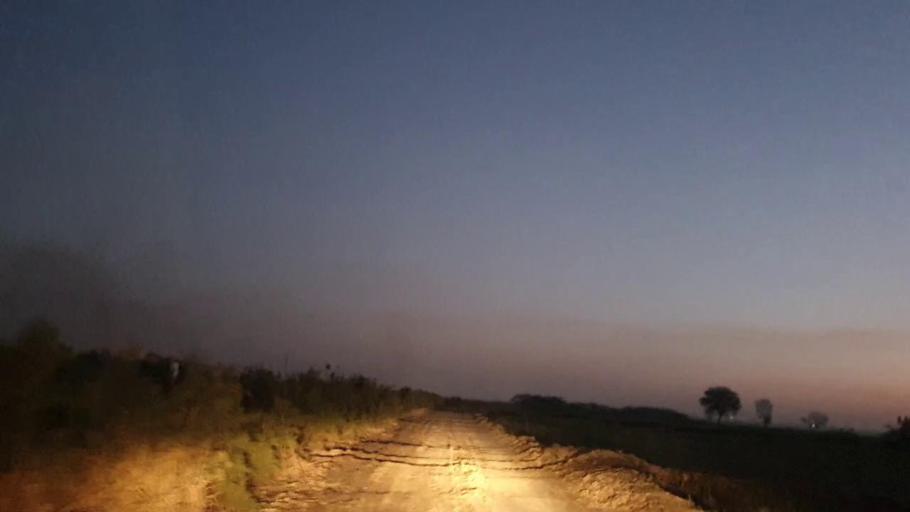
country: PK
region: Sindh
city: Nawabshah
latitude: 26.3259
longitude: 68.3772
